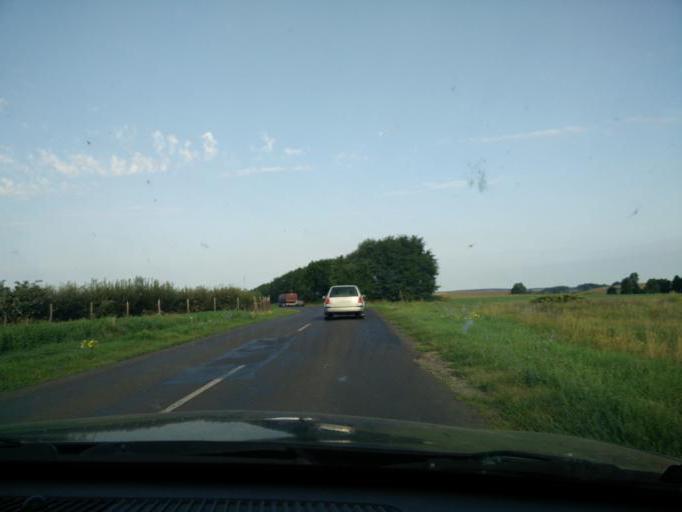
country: HU
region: Tolna
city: Nagymanyok
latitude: 46.2794
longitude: 18.4488
